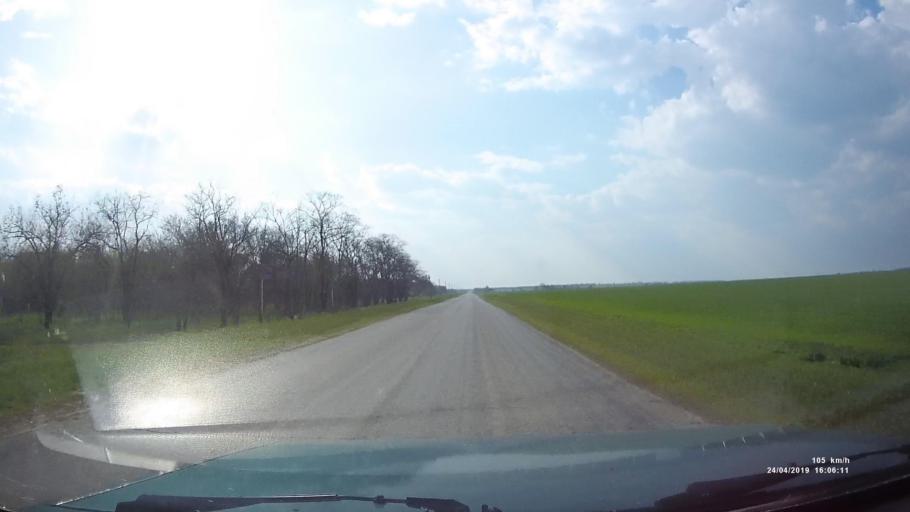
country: RU
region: Rostov
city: Sovetskoye
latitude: 46.6851
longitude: 42.3543
